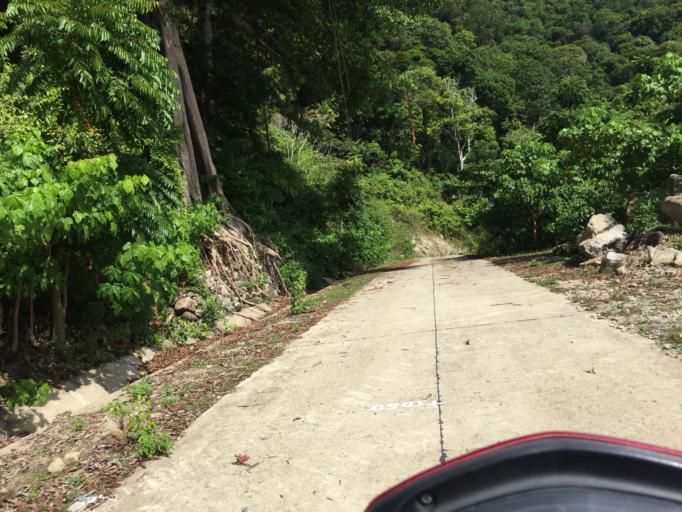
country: VN
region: Quang Nam
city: Hoi An
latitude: 15.9490
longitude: 108.5309
